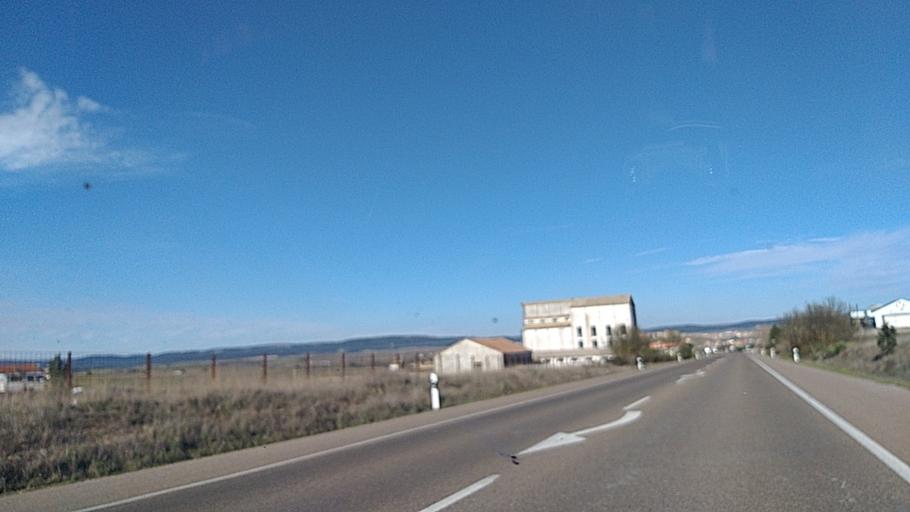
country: ES
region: Castille and Leon
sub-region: Provincia de Salamanca
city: Ciudad Rodrigo
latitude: 40.5797
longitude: -6.5594
